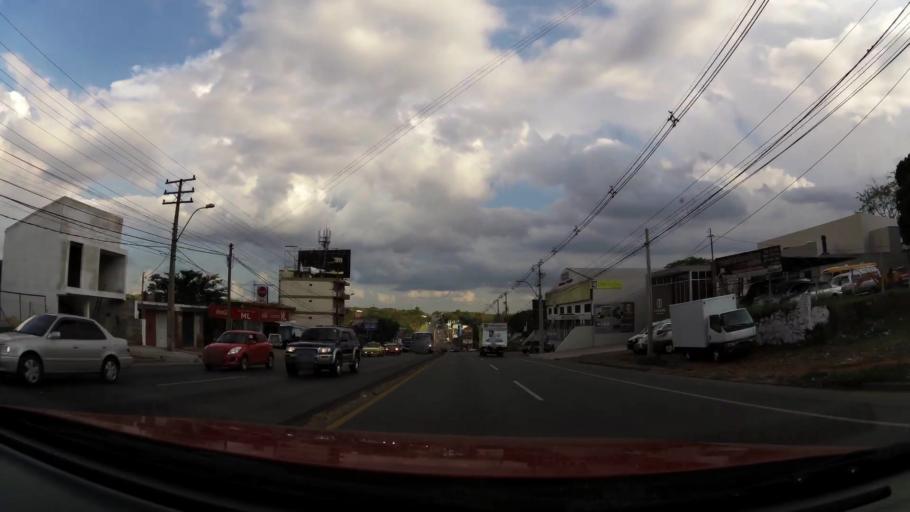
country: PY
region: Central
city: Villa Elisa
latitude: -25.3583
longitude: -57.5687
